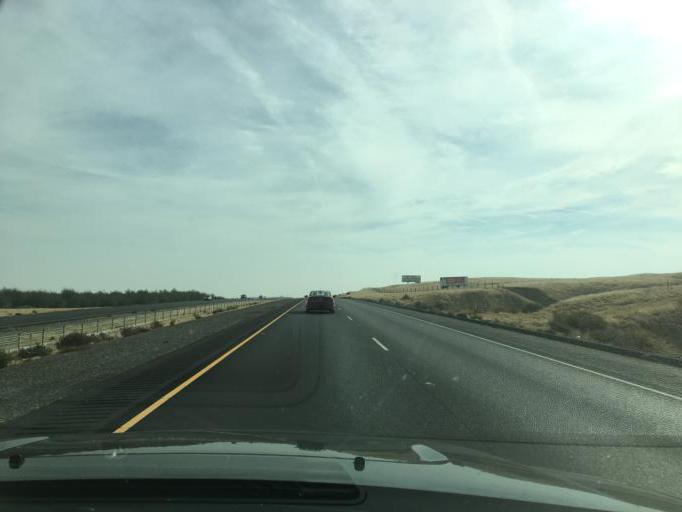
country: US
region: California
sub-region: Kings County
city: Avenal
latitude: 36.0532
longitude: -120.0631
